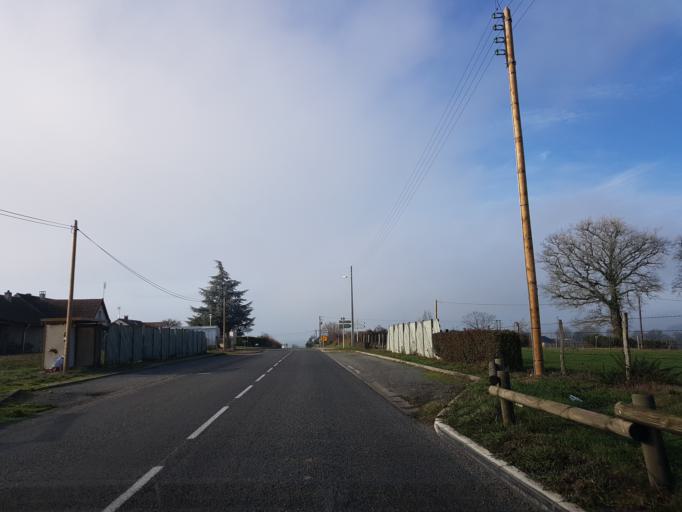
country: FR
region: Bourgogne
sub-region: Departement de Saone-et-Loire
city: Gueugnon
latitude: 46.5978
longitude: 3.9974
